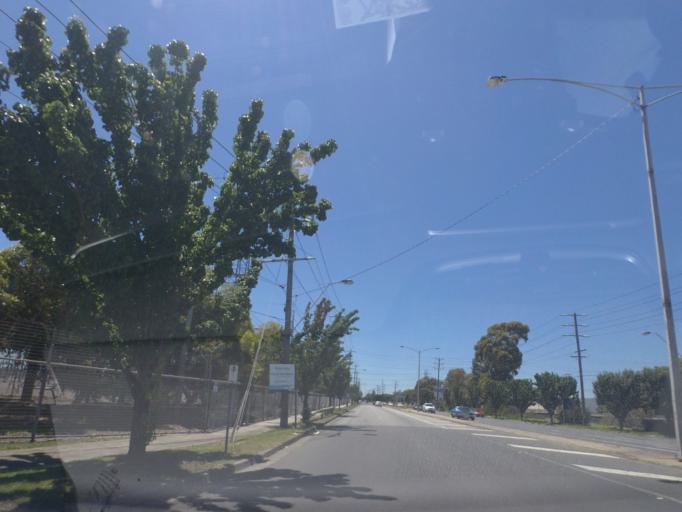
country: AU
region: Victoria
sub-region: Whittlesea
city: Thomastown
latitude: -37.6947
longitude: 145.0113
